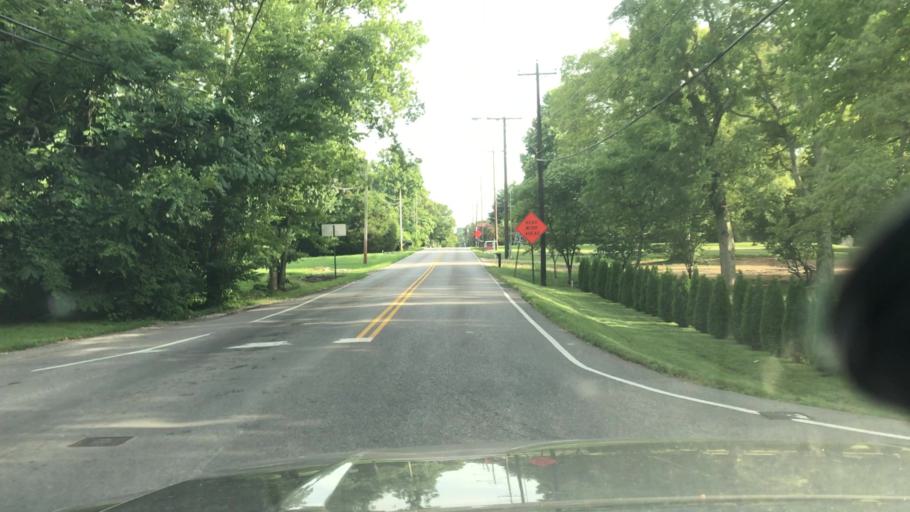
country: US
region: Tennessee
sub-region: Davidson County
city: Belle Meade
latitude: 36.1096
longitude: -86.8374
